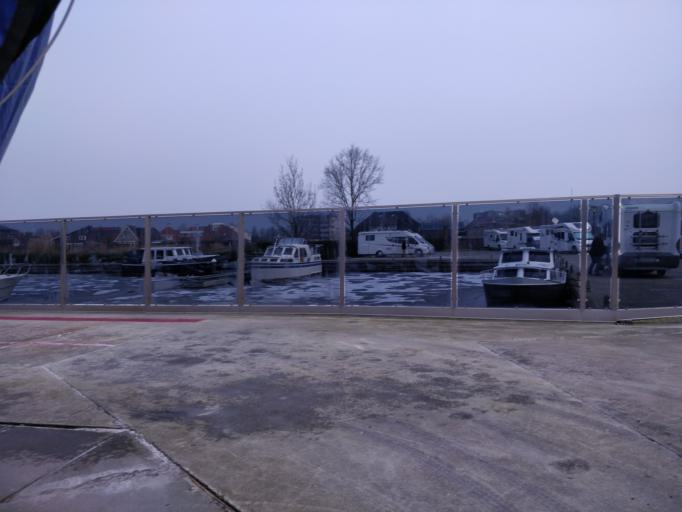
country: NL
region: Friesland
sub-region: Gemeente Leeuwarden
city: Camminghaburen
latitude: 53.1843
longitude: 5.8369
